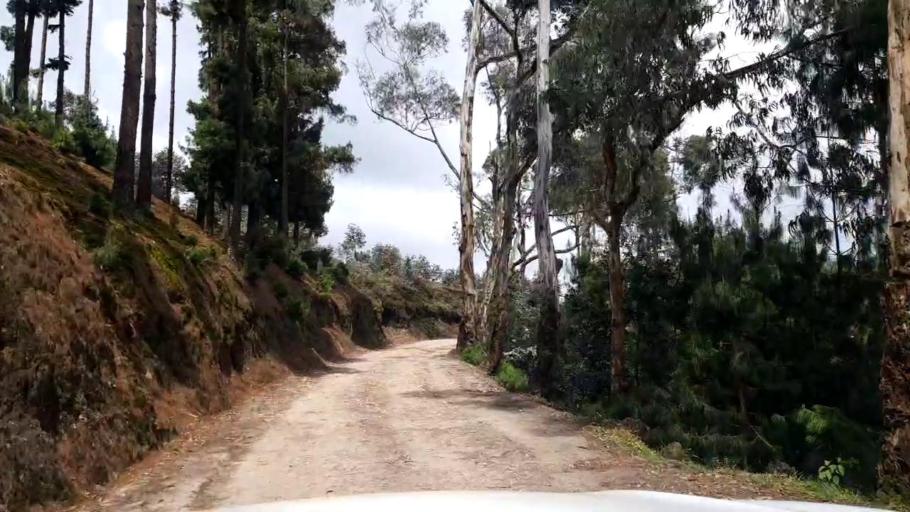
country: RW
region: Western Province
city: Kibuye
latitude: -1.9379
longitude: 29.4600
